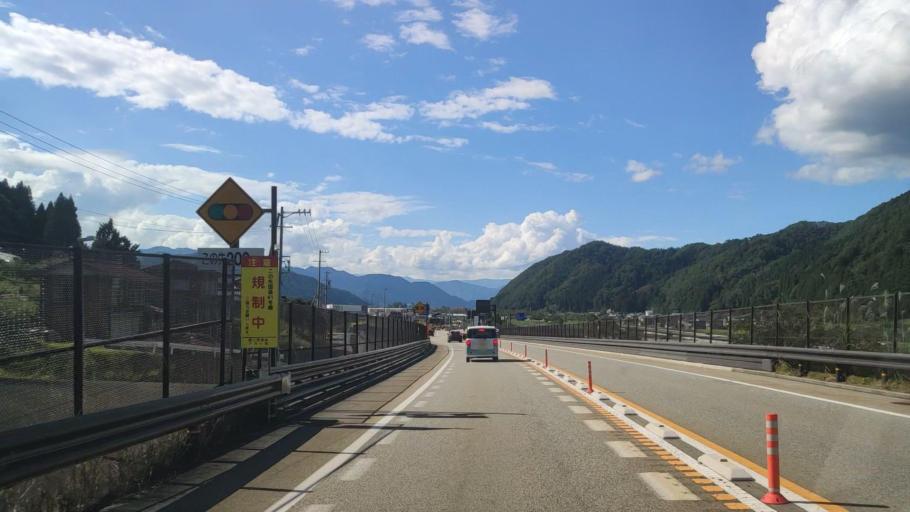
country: JP
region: Gifu
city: Takayama
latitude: 36.1998
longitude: 137.2337
